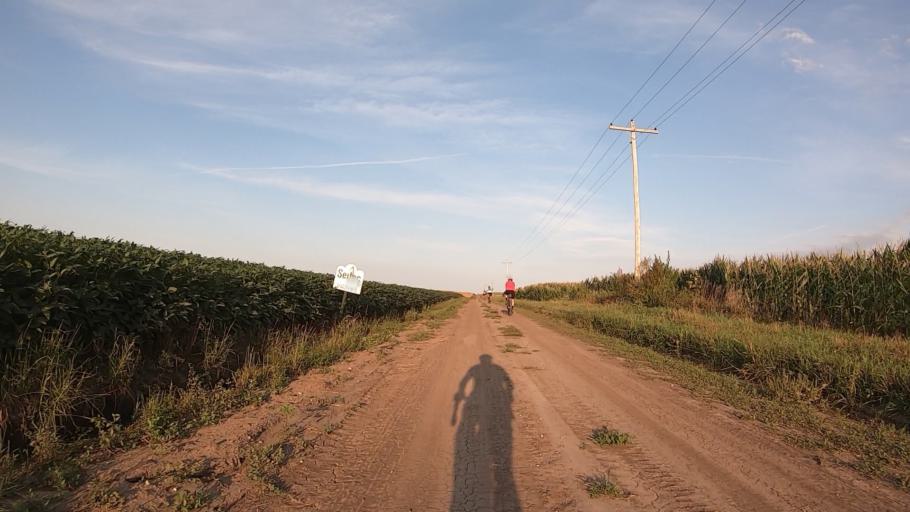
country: US
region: Kansas
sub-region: Marshall County
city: Marysville
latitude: 39.7694
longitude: -96.7213
